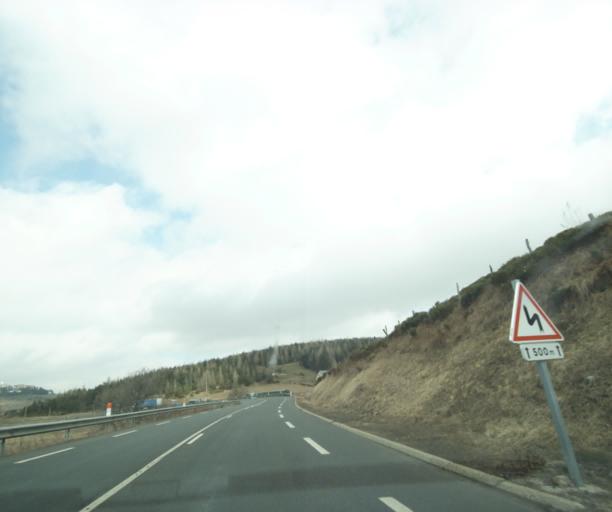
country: FR
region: Languedoc-Roussillon
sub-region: Departement de la Lozere
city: Mende
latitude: 44.6255
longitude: 3.6745
